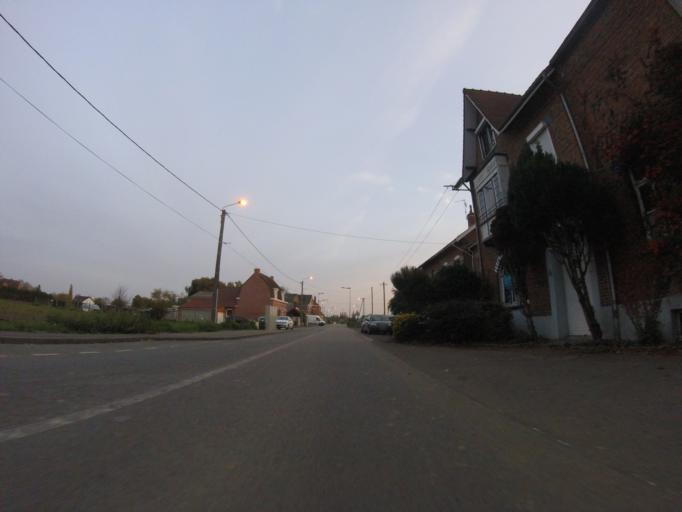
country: FR
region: Nord-Pas-de-Calais
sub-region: Departement du Pas-de-Calais
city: Sailly-sur-la-Lys
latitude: 50.6458
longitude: 2.7838
